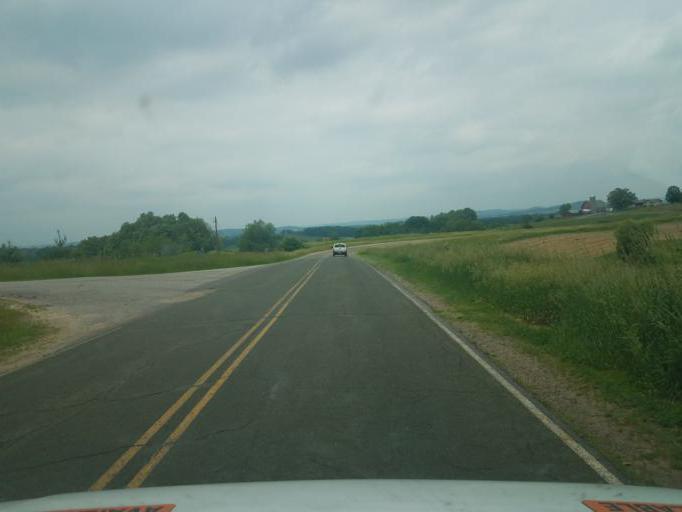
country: US
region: Wisconsin
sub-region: Vernon County
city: Hillsboro
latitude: 43.6479
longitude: -90.2921
